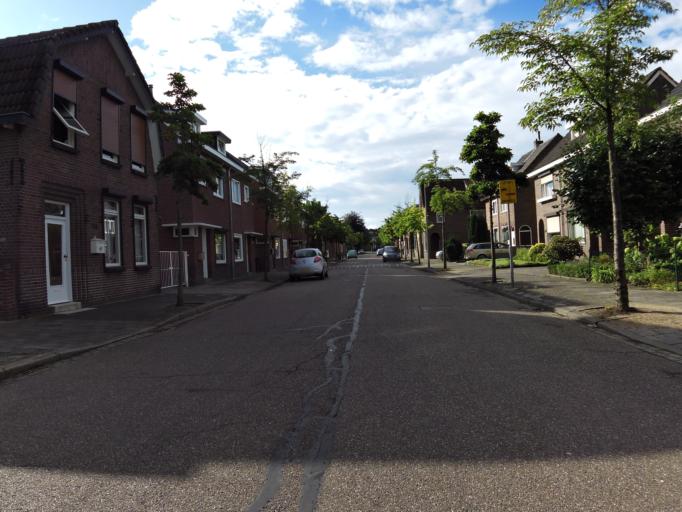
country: NL
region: Limburg
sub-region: Gemeente Heerlen
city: Nieuw-Lotbroek
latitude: 50.9169
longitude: 5.9244
